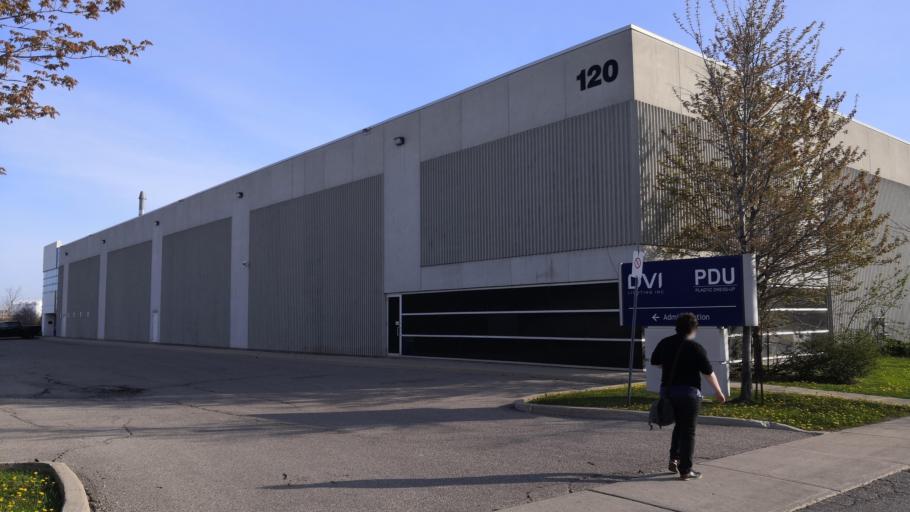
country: CA
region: Ontario
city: Concord
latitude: 43.7915
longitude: -79.4924
